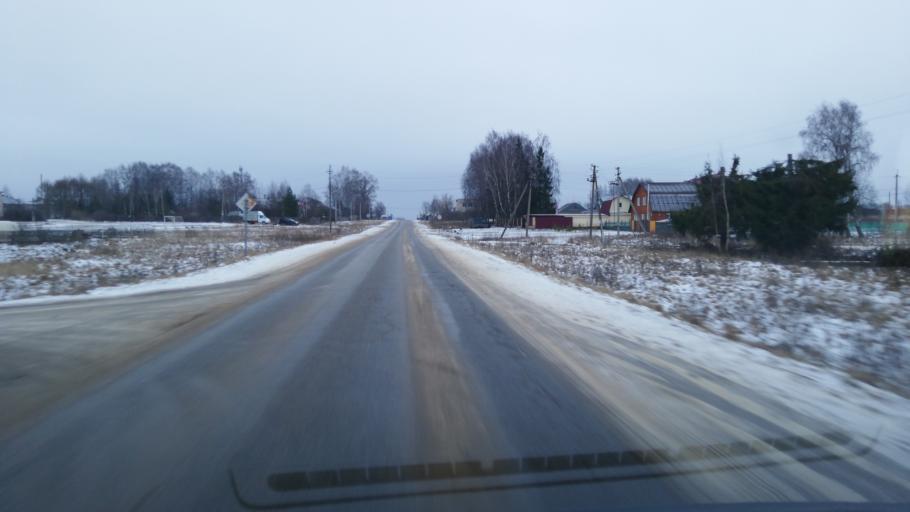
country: RU
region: Kostroma
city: Oktyabr'skiy
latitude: 57.7158
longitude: 41.1453
